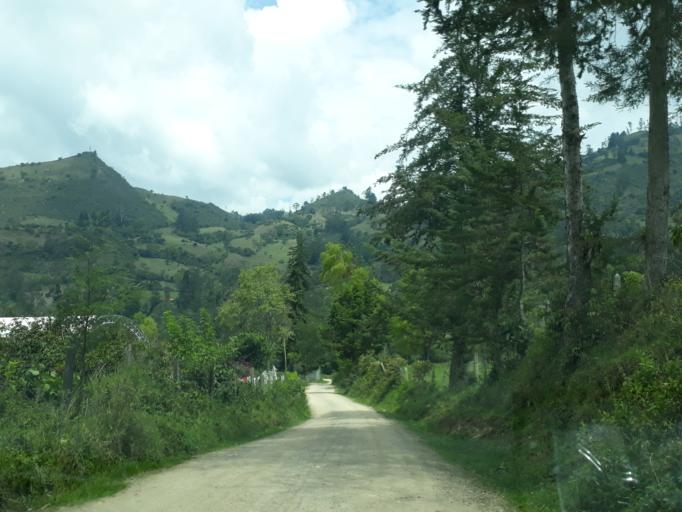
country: CO
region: Cundinamarca
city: Macheta
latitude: 5.0957
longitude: -73.5661
